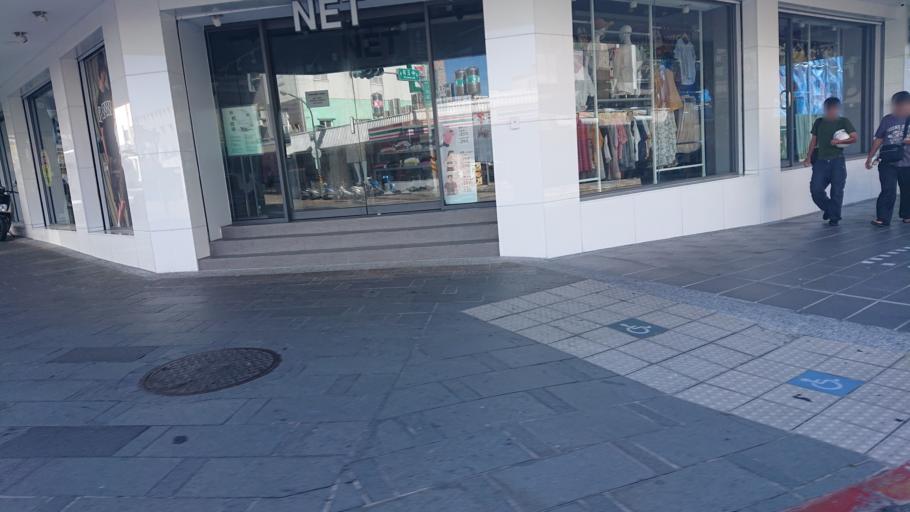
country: TW
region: Taiwan
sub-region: Penghu
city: Ma-kung
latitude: 23.5656
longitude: 119.5654
